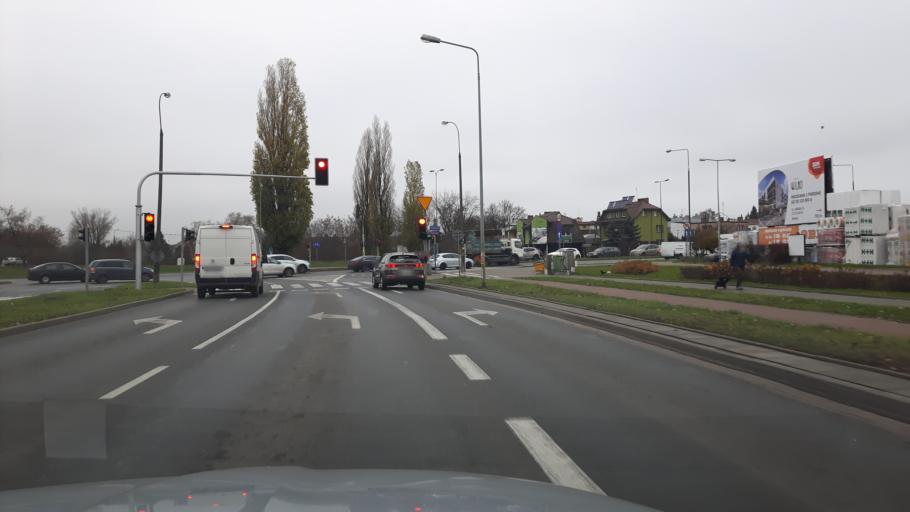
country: PL
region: Masovian Voivodeship
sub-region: Warszawa
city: Targowek
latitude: 52.2748
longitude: 21.0664
